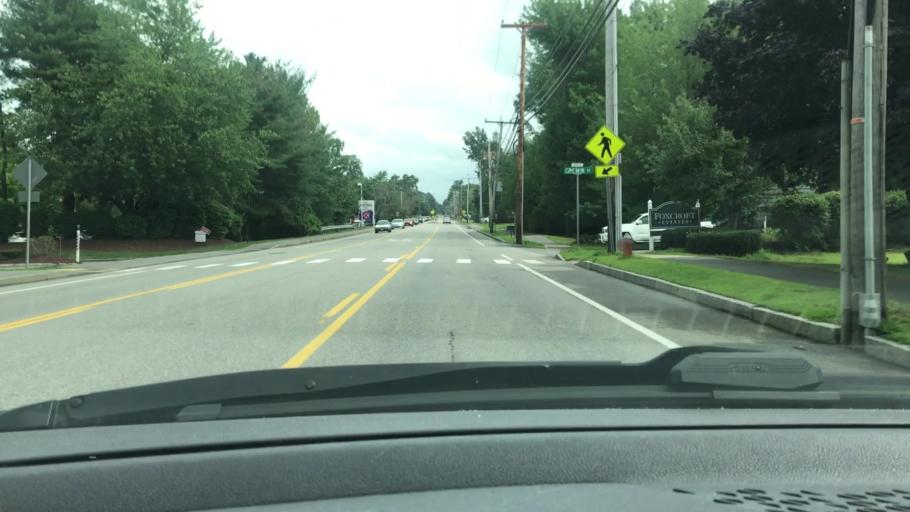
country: US
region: New Hampshire
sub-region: Merrimack County
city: East Concord
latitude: 43.2606
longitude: -71.5817
